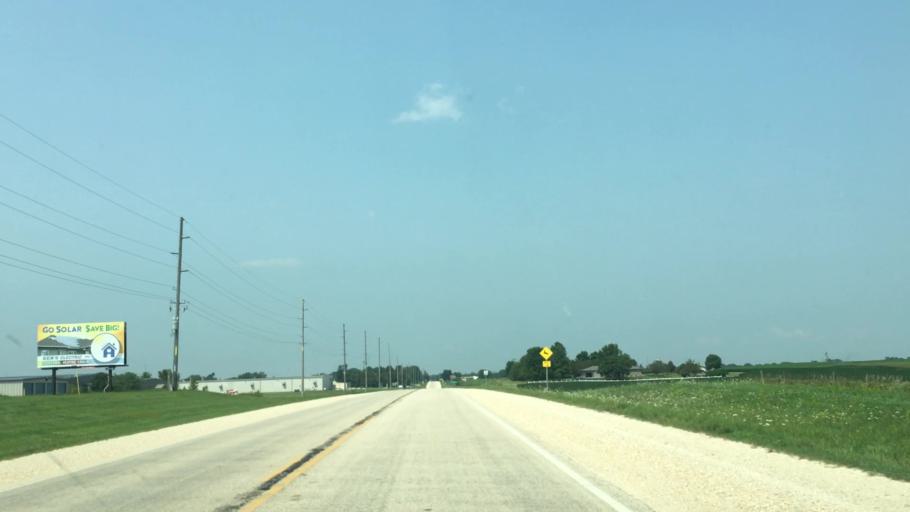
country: US
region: Iowa
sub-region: Fayette County
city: West Union
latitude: 42.9383
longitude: -91.8142
